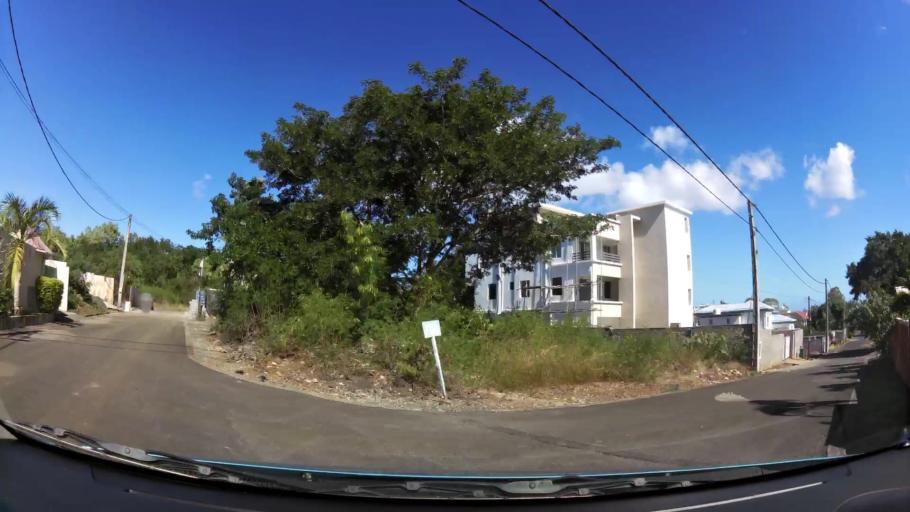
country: MU
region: Black River
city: Flic en Flac
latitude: -20.2852
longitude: 57.3730
